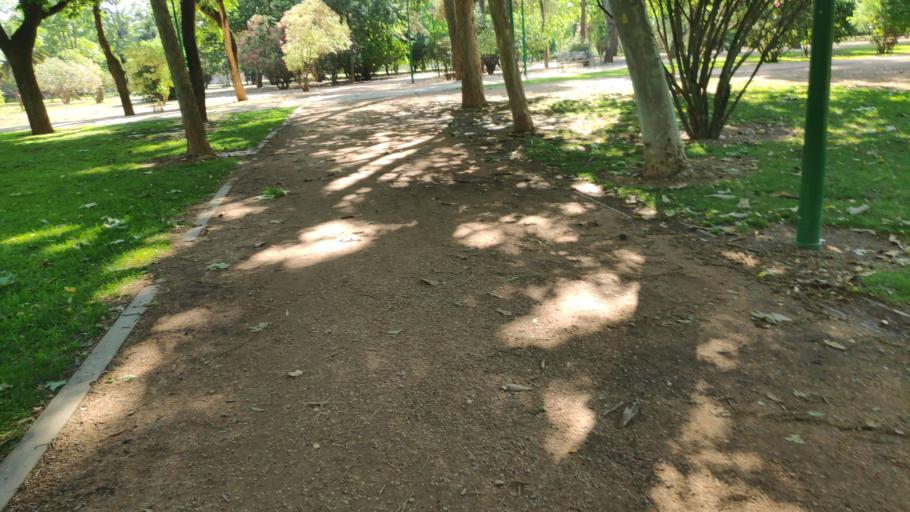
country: ES
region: Andalusia
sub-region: Province of Cordoba
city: Cordoba
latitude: 37.8717
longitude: -4.7897
